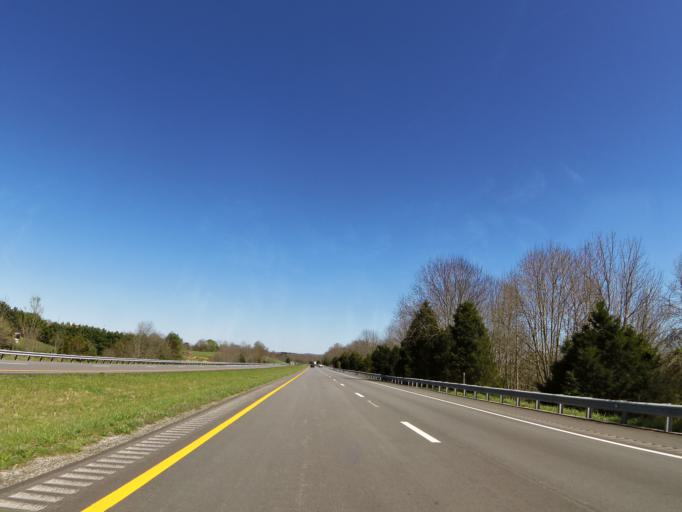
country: US
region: Kentucky
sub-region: Pulaski County
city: Somerset
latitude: 37.0978
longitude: -84.7578
